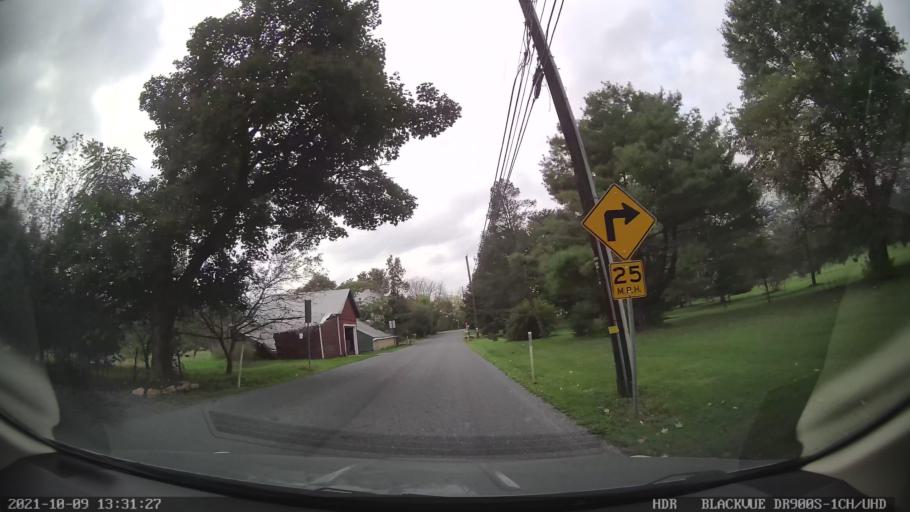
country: US
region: Pennsylvania
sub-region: Lehigh County
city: Alburtis
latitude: 40.5272
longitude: -75.6126
